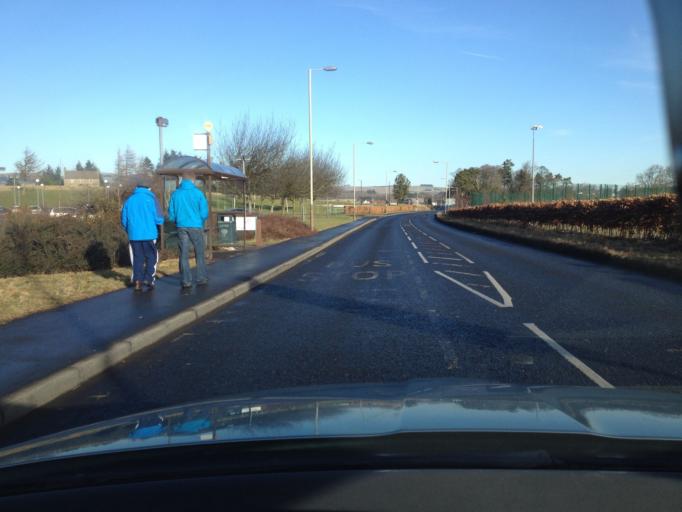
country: GB
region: Scotland
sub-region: Perth and Kinross
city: Milnathort
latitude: 56.2173
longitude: -3.4264
